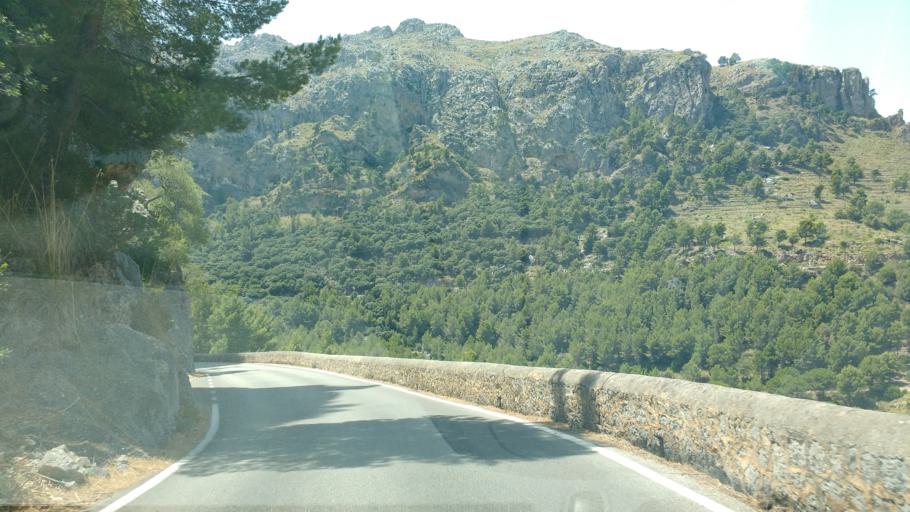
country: ES
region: Balearic Islands
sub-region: Illes Balears
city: Escorca
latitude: 39.8439
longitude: 2.7989
